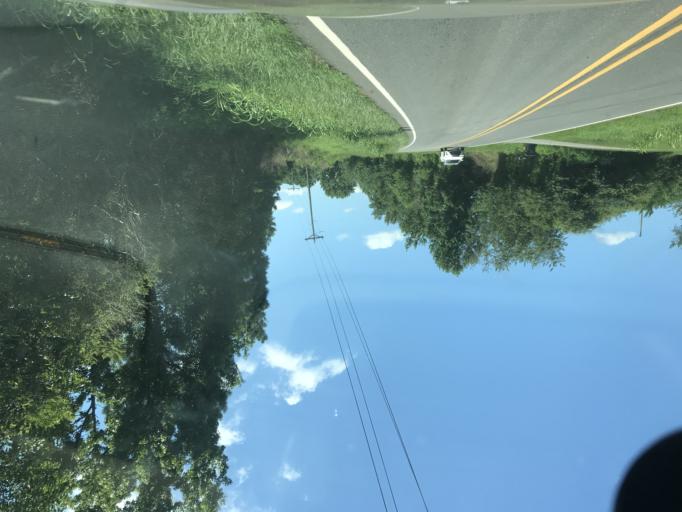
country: US
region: Georgia
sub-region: Dawson County
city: Dawsonville
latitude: 34.3306
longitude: -84.0488
